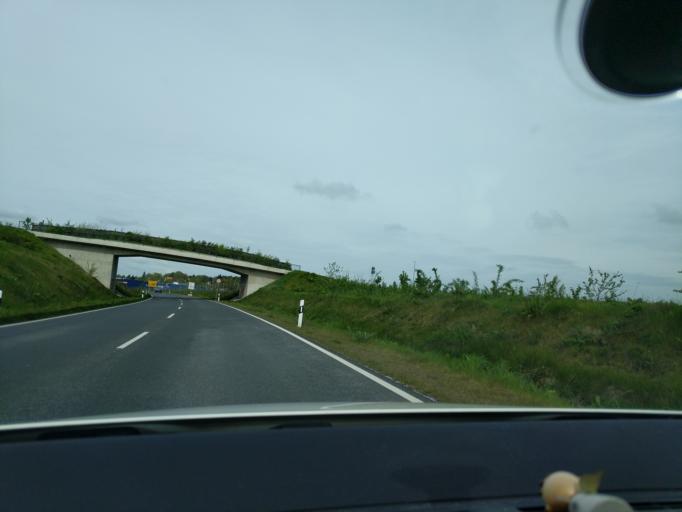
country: DE
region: Saxony
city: Bannewitz
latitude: 50.9897
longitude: 13.7209
